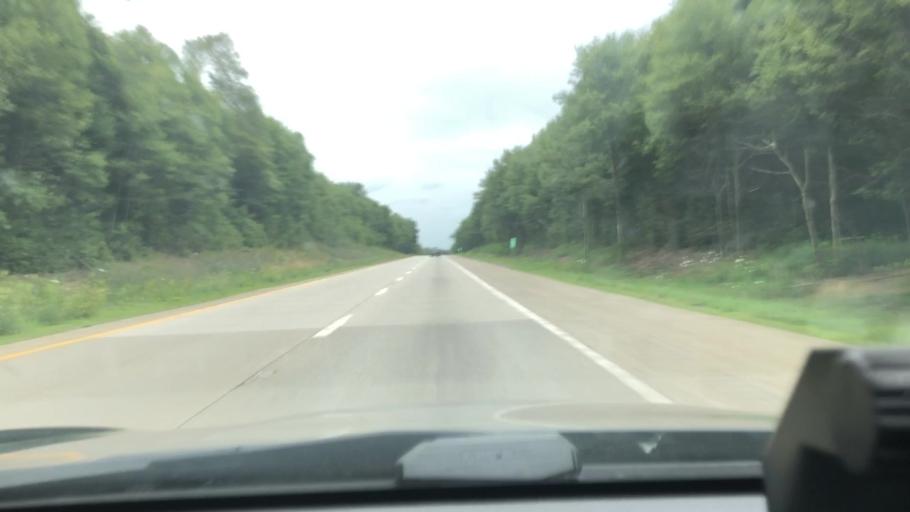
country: US
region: Pennsylvania
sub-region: Monroe County
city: Mount Pocono
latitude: 41.1508
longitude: -75.4095
